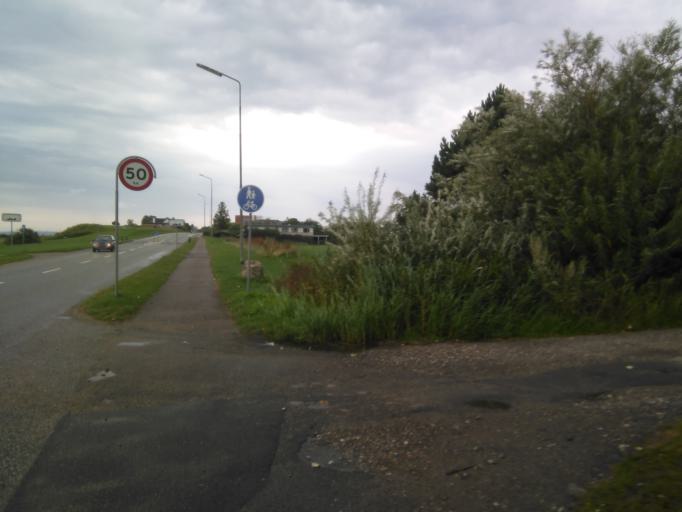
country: DK
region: Central Jutland
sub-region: Arhus Kommune
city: Hjortshoj
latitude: 56.2234
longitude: 10.3009
